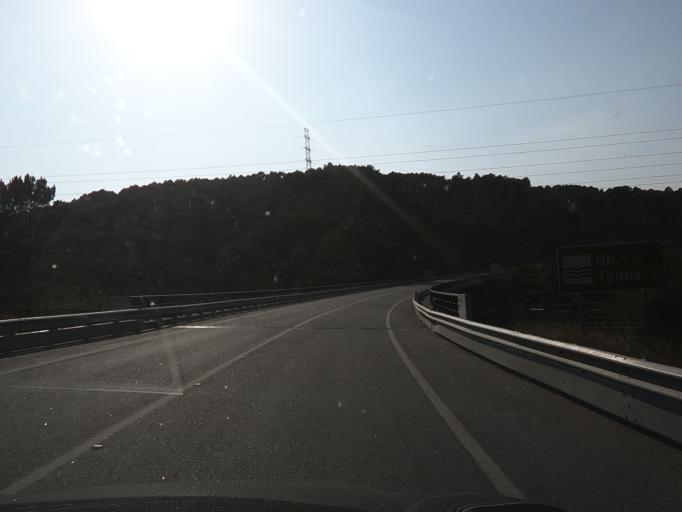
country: PT
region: Vila Real
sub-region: Sabrosa
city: Vilela
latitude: 41.2632
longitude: -7.6699
